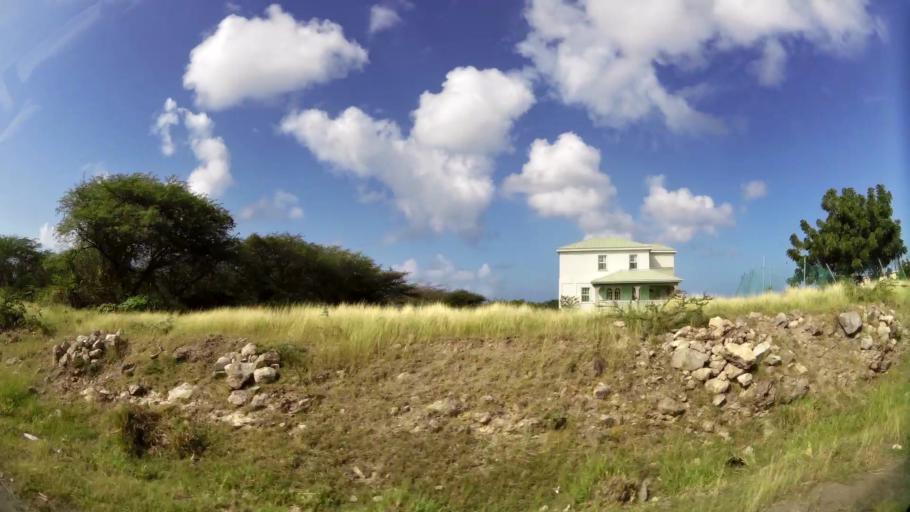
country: KN
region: Saint Paul Charlestown
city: Charlestown
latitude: 17.1265
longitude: -62.6193
